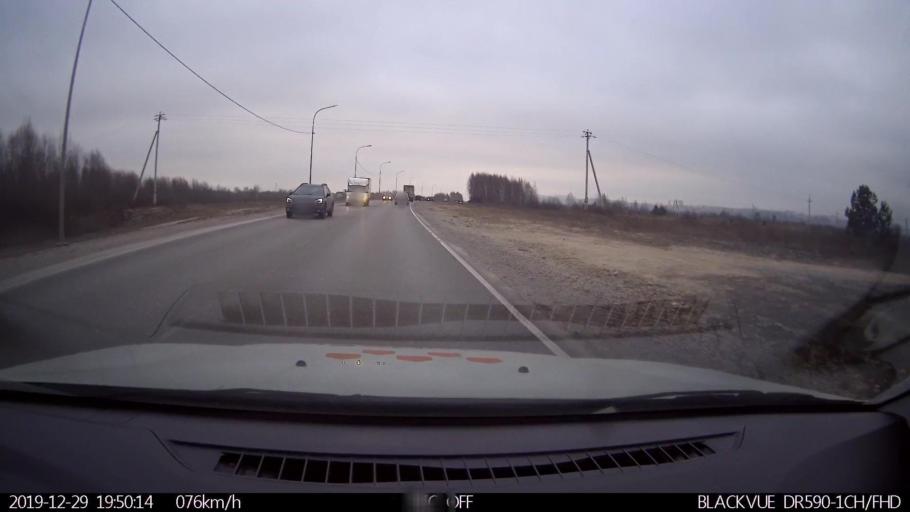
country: RU
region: Nizjnij Novgorod
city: Nizhniy Novgorod
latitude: 56.3700
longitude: 44.0255
